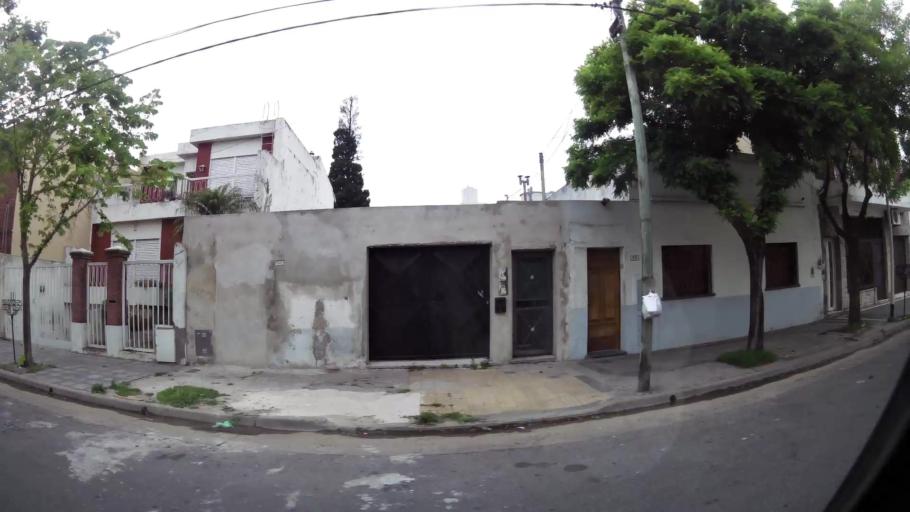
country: AR
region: Buenos Aires
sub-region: Partido de Lanus
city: Lanus
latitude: -34.6770
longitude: -58.3885
